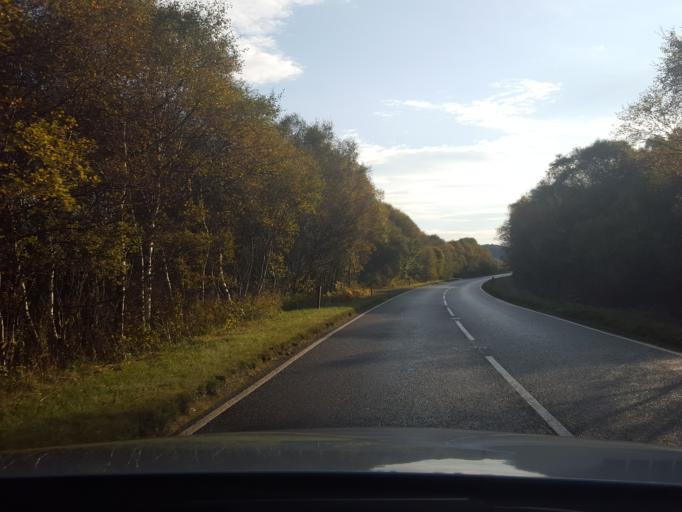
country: GB
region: Scotland
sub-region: Highland
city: Portree
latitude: 57.2625
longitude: -5.9485
